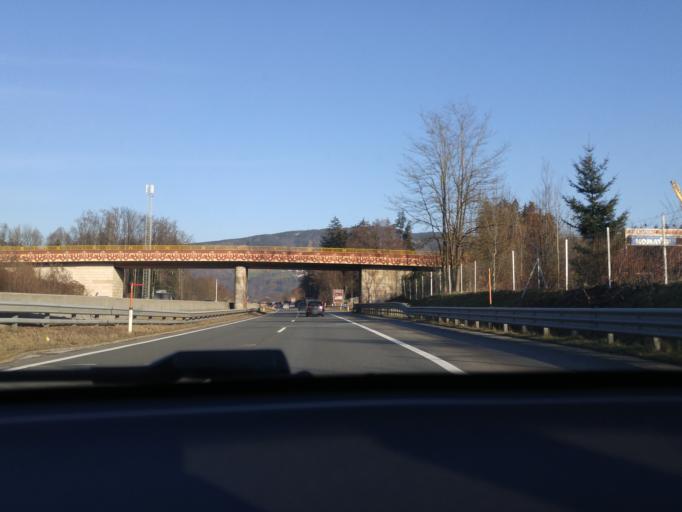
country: AT
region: Upper Austria
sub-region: Politischer Bezirk Vocklabruck
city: Mondsee
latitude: 47.8469
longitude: 13.3174
